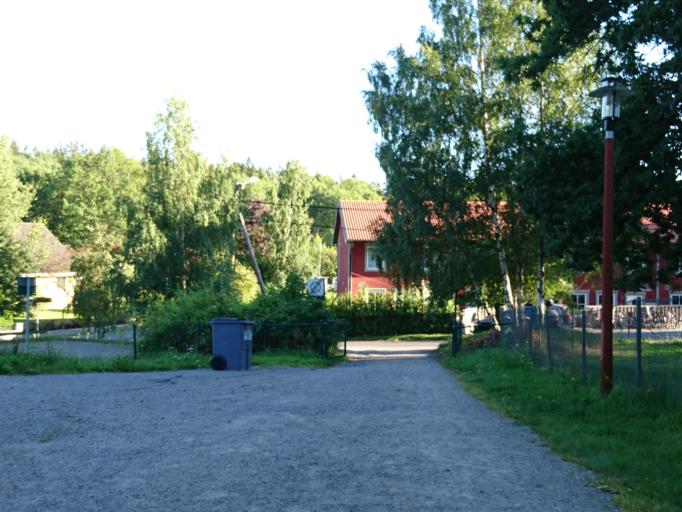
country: SE
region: Stockholm
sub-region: Huddinge Kommun
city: Segeltorp
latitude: 59.2725
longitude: 17.9290
